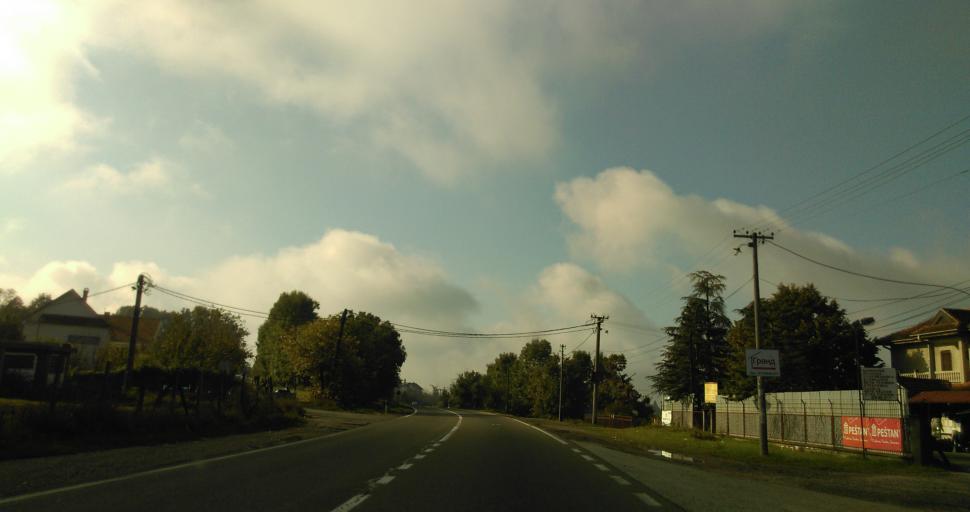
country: RS
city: Vranic
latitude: 44.5993
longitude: 20.3520
